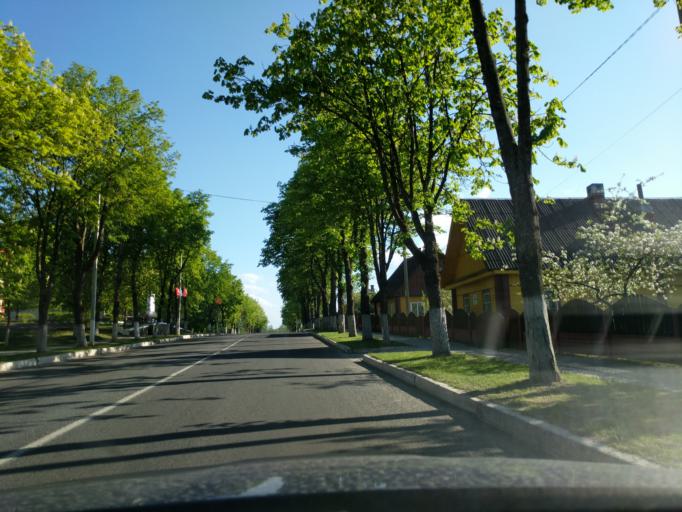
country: BY
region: Minsk
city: Myadzyel
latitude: 54.8665
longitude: 26.9339
